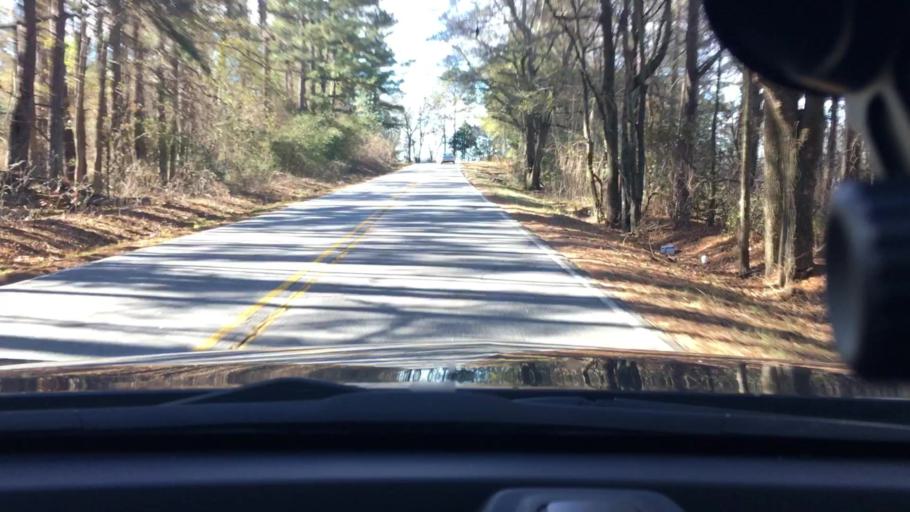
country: US
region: South Carolina
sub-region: Spartanburg County
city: Spartanburg
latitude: 34.9257
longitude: -81.8596
